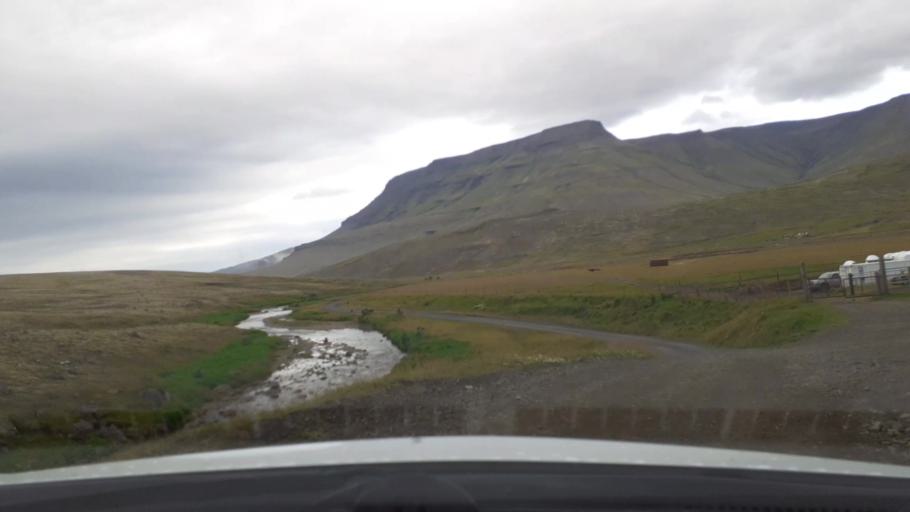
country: IS
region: Capital Region
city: Mosfellsbaer
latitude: 64.2070
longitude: -21.5672
